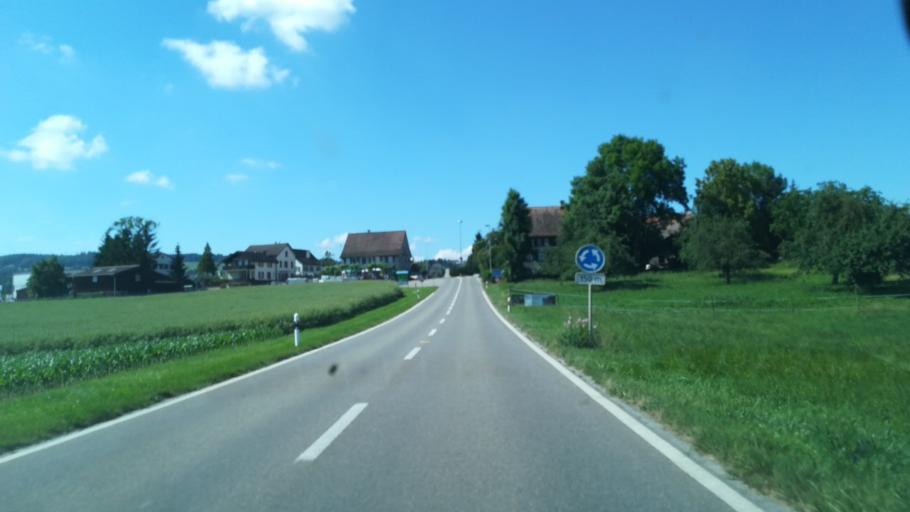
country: CH
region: Thurgau
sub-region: Weinfelden District
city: Sulgen
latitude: 47.5581
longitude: 9.1746
